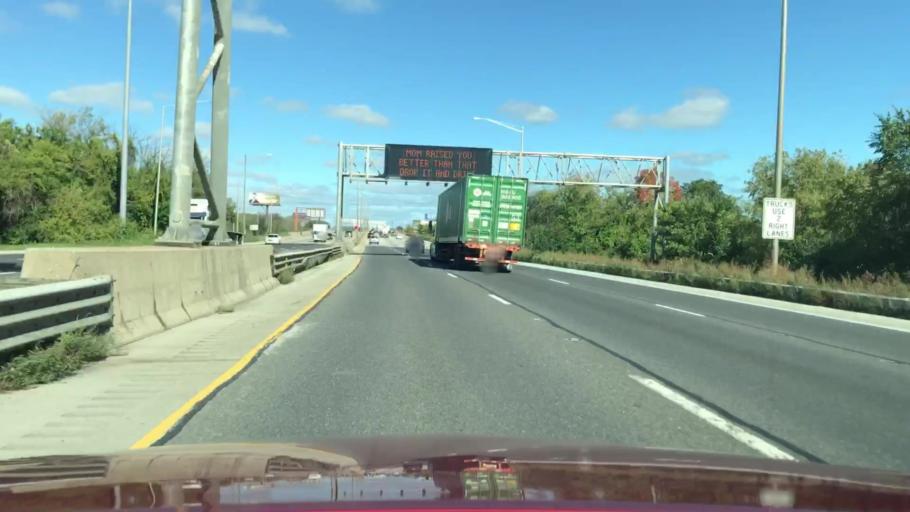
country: US
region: Illinois
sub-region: Cook County
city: Burnham
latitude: 41.6312
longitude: -87.5783
